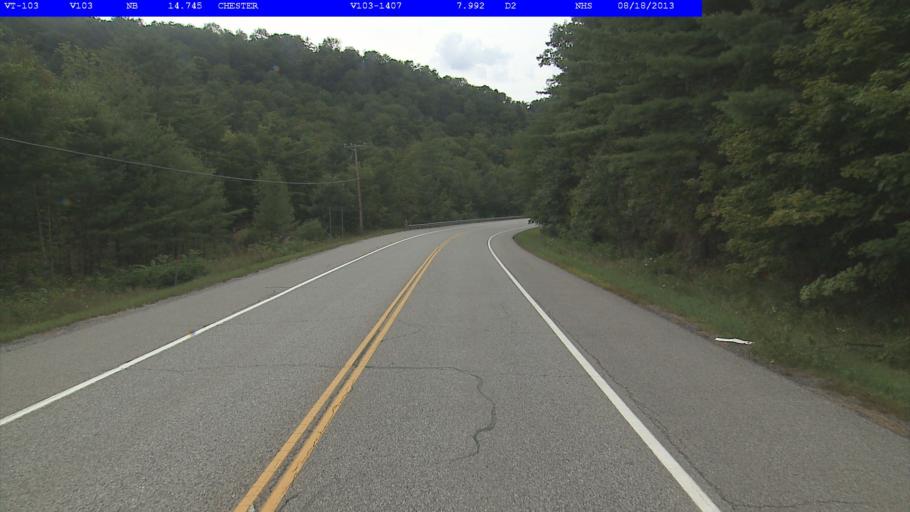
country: US
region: Vermont
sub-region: Windsor County
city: Chester
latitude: 43.3269
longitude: -72.6127
